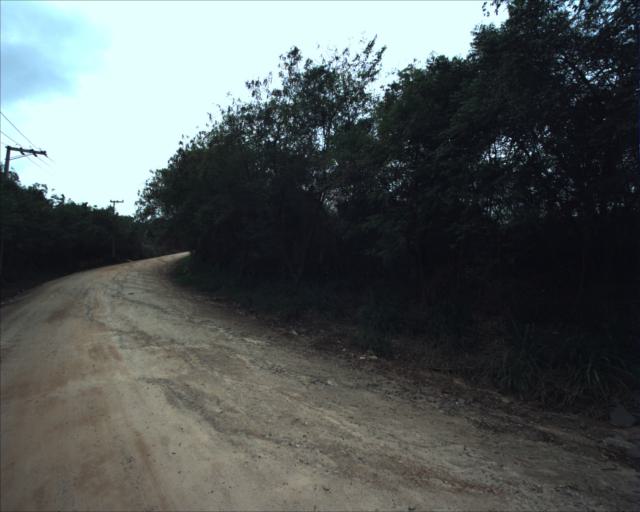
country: BR
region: Sao Paulo
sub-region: Sorocaba
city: Sorocaba
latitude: -23.4578
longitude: -47.3884
